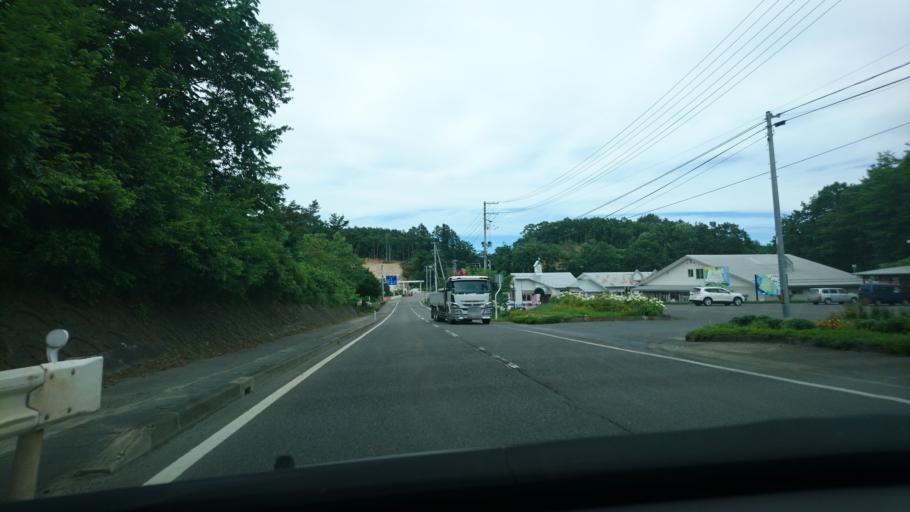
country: JP
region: Iwate
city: Miyako
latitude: 39.9469
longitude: 141.8418
